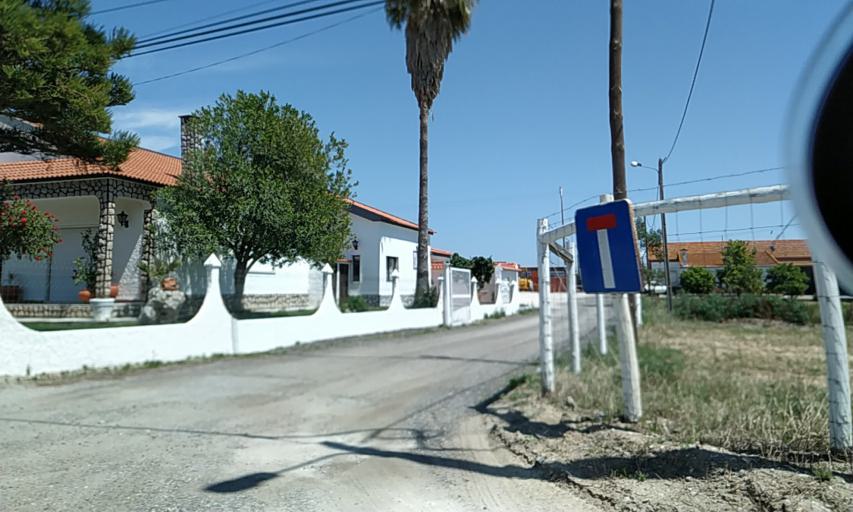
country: PT
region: Santarem
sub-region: Benavente
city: Poceirao
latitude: 38.6746
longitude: -8.7345
